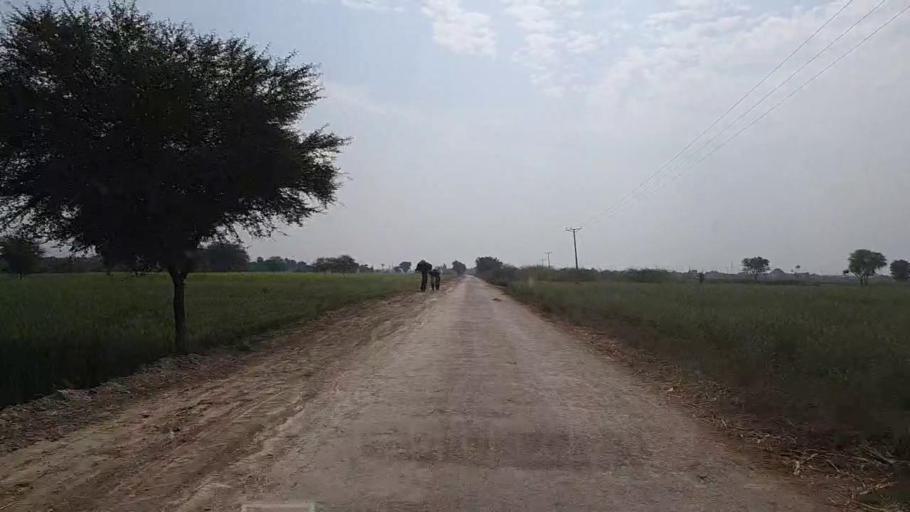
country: PK
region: Sindh
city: Mirwah Gorchani
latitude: 25.3458
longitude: 69.0536
